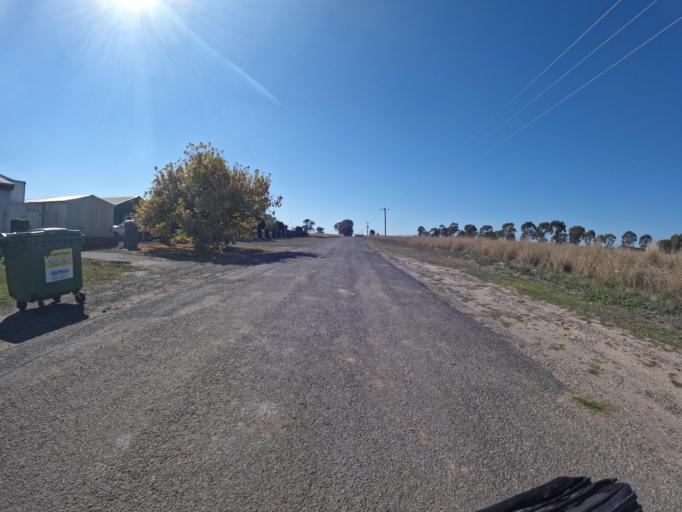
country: AU
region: Victoria
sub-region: Greater Bendigo
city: Epsom
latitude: -36.7895
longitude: 144.5132
